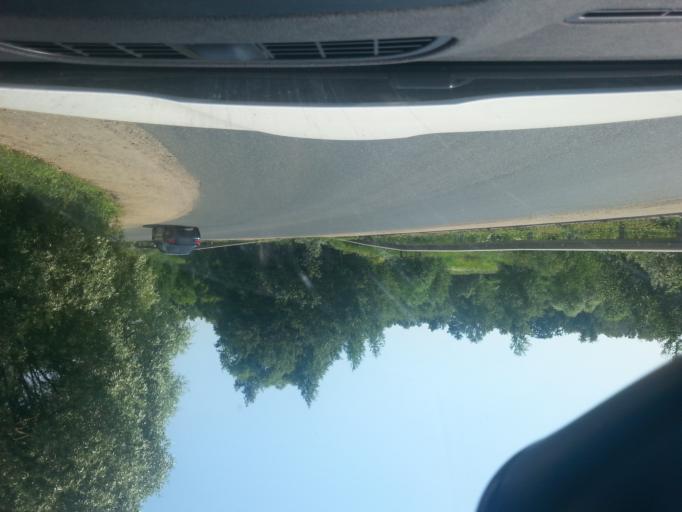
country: RU
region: Moskovskaya
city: Korenevo
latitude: 55.7110
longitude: 37.9722
